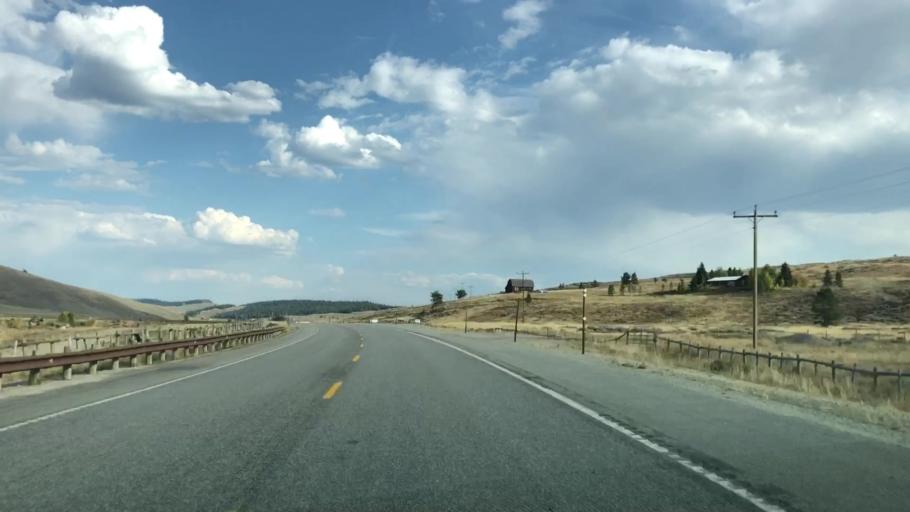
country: US
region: Wyoming
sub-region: Teton County
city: Hoback
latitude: 43.2269
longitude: -110.4318
